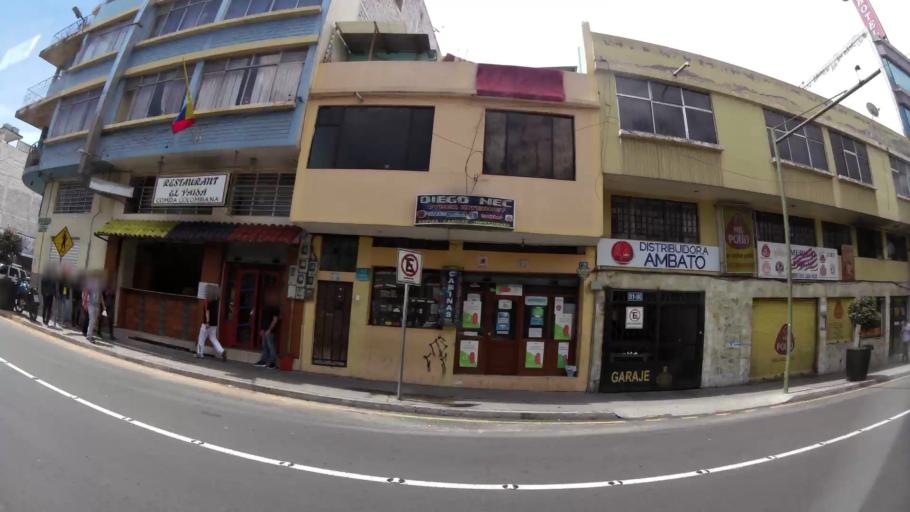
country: EC
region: Tungurahua
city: Ambato
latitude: -1.2366
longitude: -78.6199
